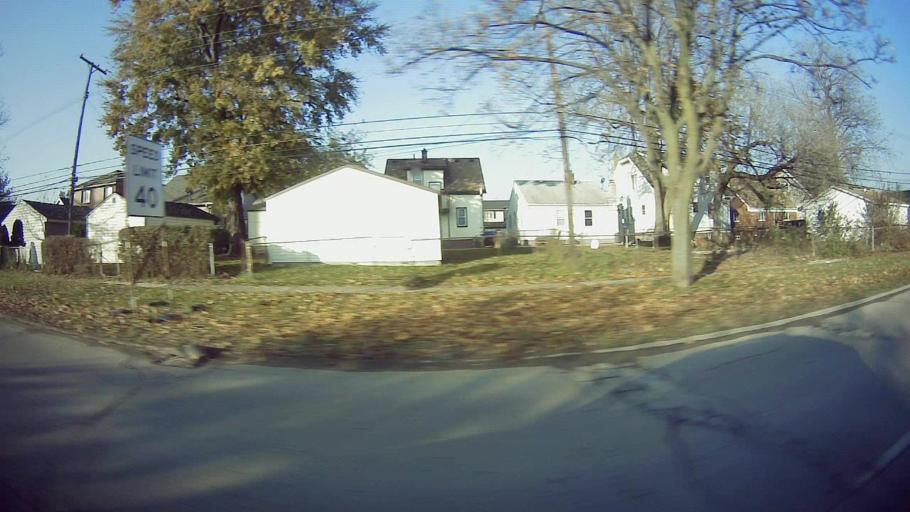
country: US
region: Michigan
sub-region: Wayne County
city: Dearborn
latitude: 42.3230
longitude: -83.1957
